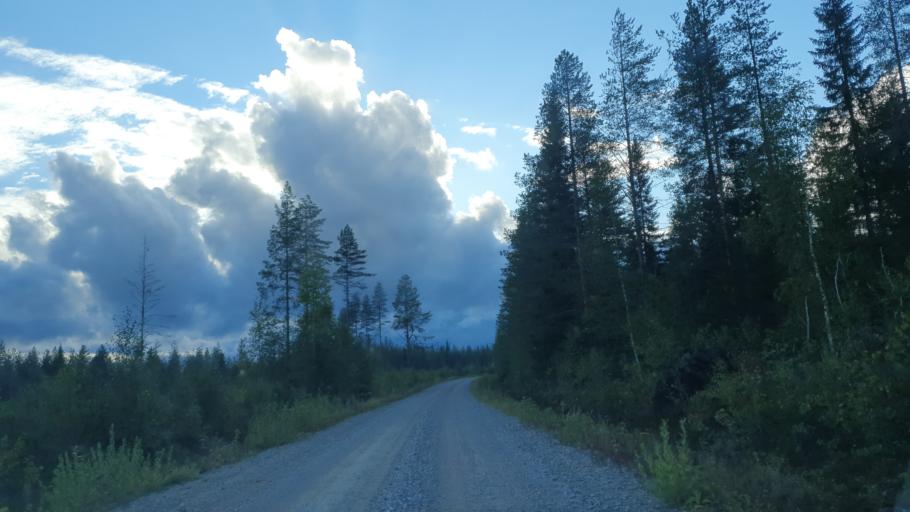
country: FI
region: Kainuu
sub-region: Kehys-Kainuu
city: Kuhmo
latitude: 64.3352
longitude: 29.9378
